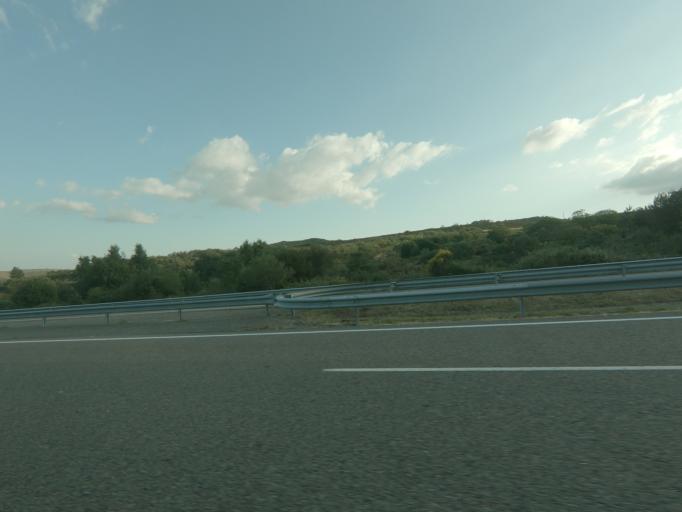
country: ES
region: Galicia
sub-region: Provincia de Ourense
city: Cualedro
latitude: 41.9881
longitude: -7.5520
